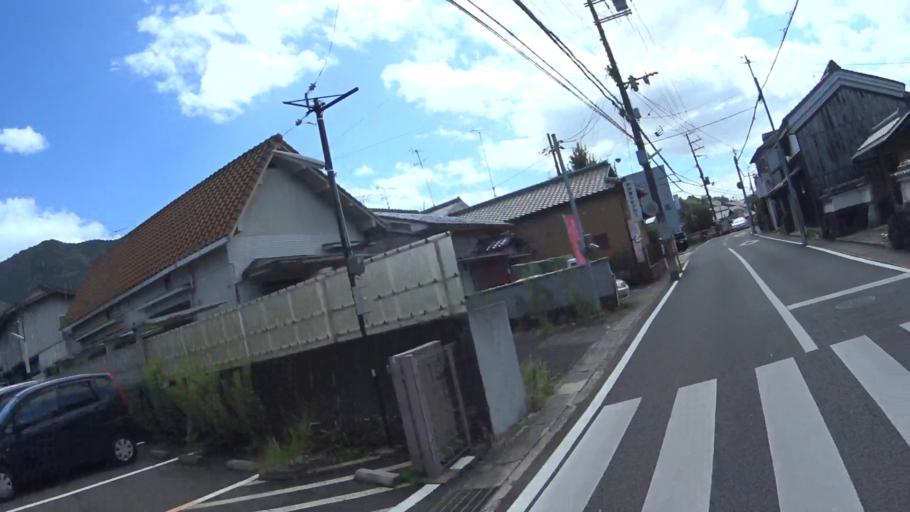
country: JP
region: Kyoto
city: Uji
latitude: 34.9480
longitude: 135.8171
